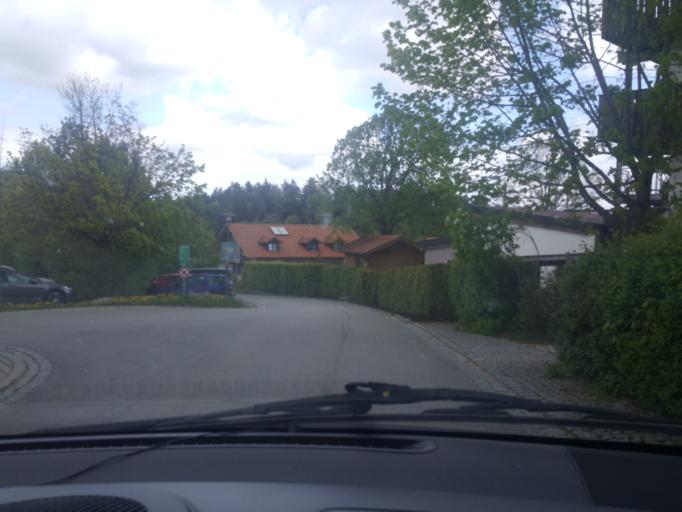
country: DE
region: Bavaria
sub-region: Lower Bavaria
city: Kollnburg
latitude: 49.0482
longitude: 12.8618
